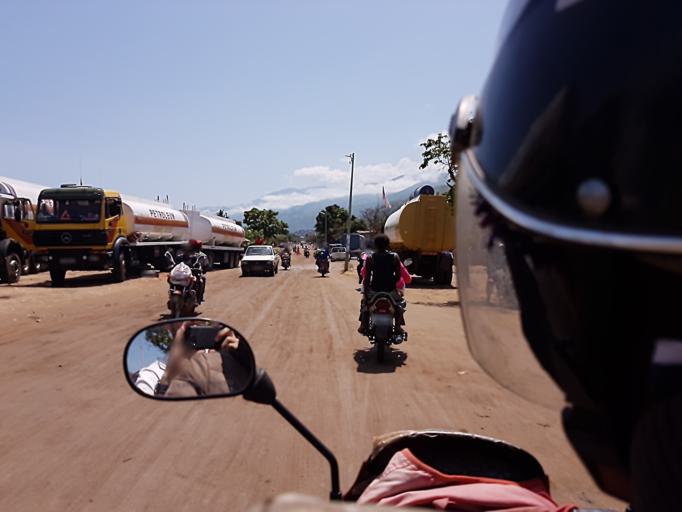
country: CD
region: South Kivu
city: Uvira
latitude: -3.3636
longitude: 29.1496
